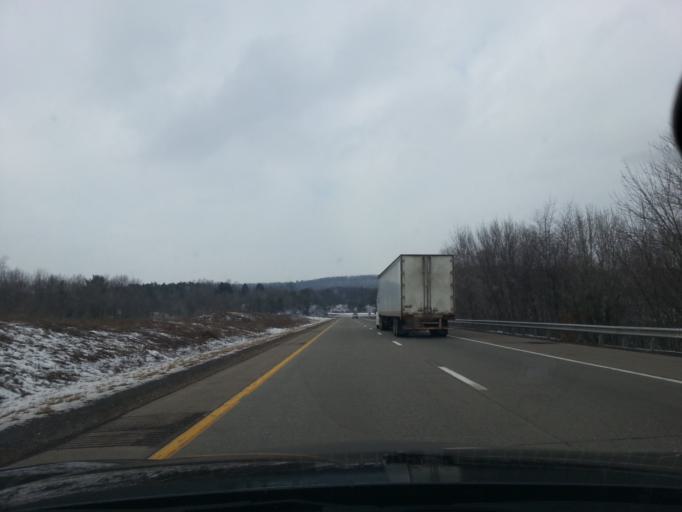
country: US
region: Pennsylvania
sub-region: Luzerne County
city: Conyngham
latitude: 41.0372
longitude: -76.0134
